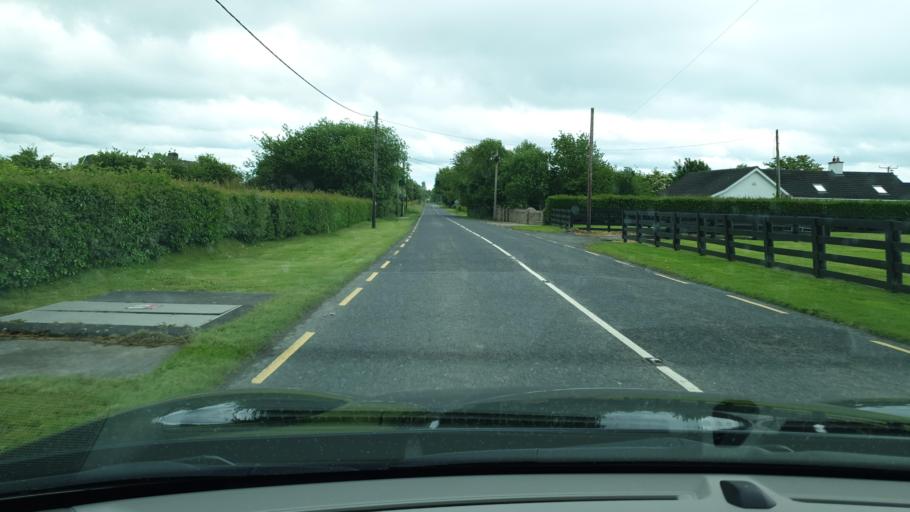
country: IE
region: Leinster
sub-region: An Mhi
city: Dunboyne
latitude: 53.4308
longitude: -6.5096
